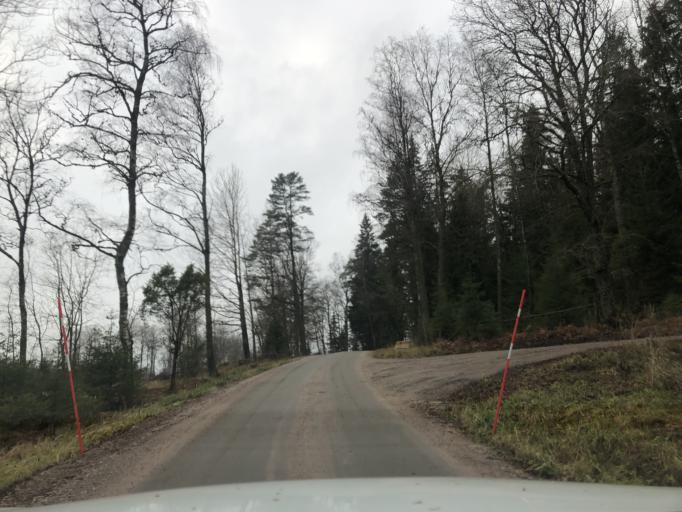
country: SE
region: Vaestra Goetaland
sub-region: Ulricehamns Kommun
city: Ulricehamn
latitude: 57.8589
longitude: 13.6143
